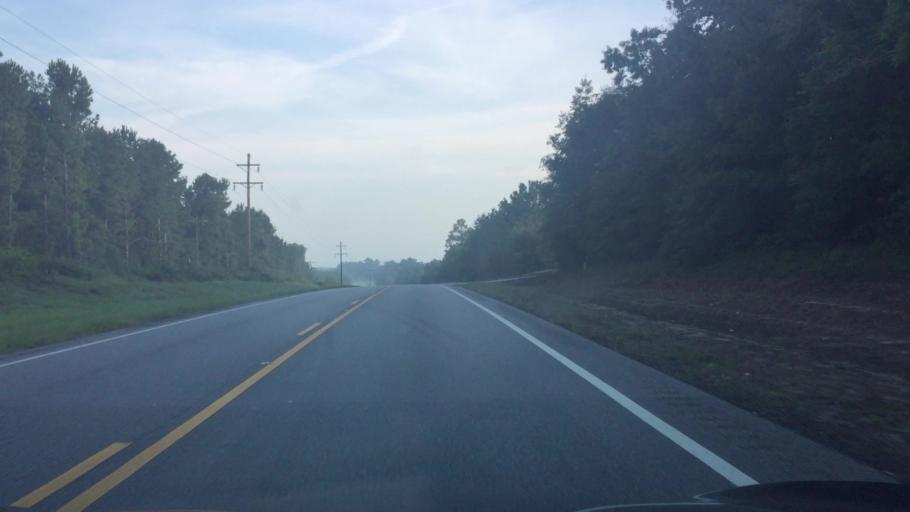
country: US
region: Alabama
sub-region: Covington County
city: Florala
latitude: 31.0687
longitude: -86.4023
